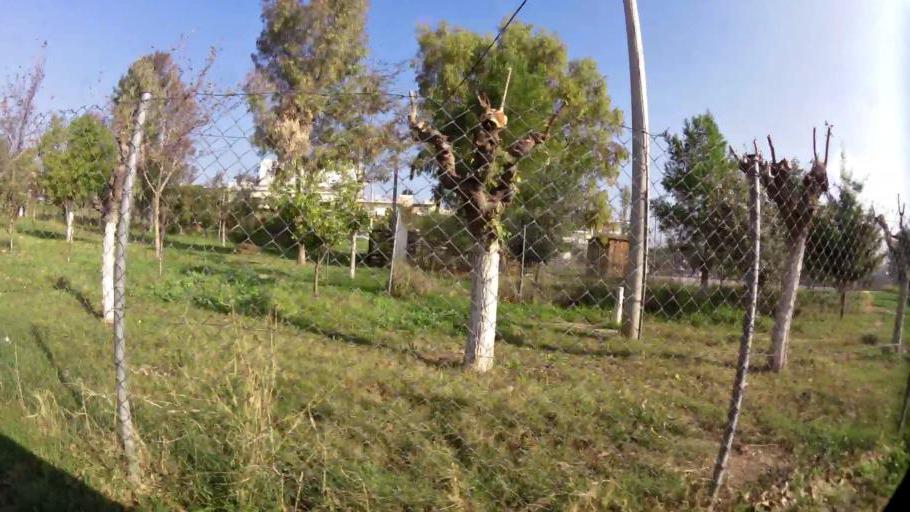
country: GR
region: Attica
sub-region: Nomarchia Athinas
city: Nea Filadelfeia
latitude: 38.0584
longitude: 23.7393
